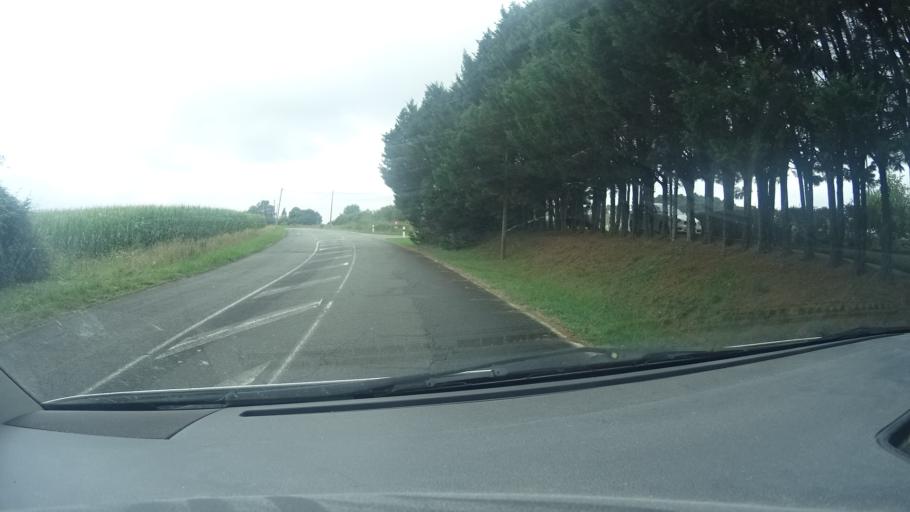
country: FR
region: Aquitaine
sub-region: Departement des Pyrenees-Atlantiques
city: Mont
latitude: 43.4862
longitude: -0.6957
